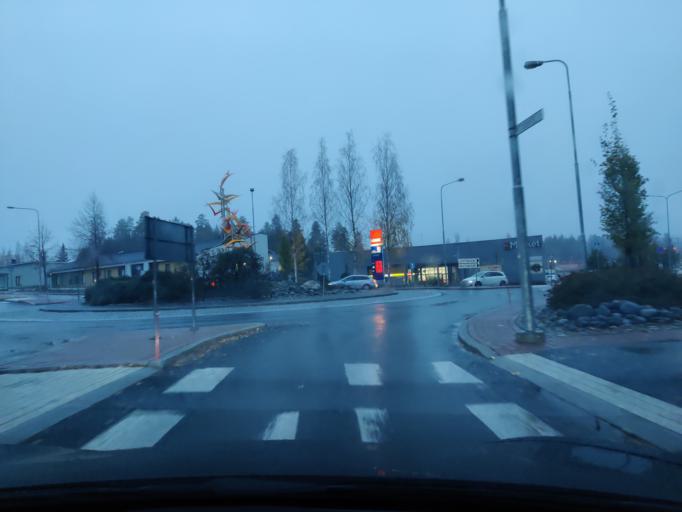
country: FI
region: Northern Savo
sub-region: Kuopio
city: Kuopio
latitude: 62.8338
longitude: 27.6667
